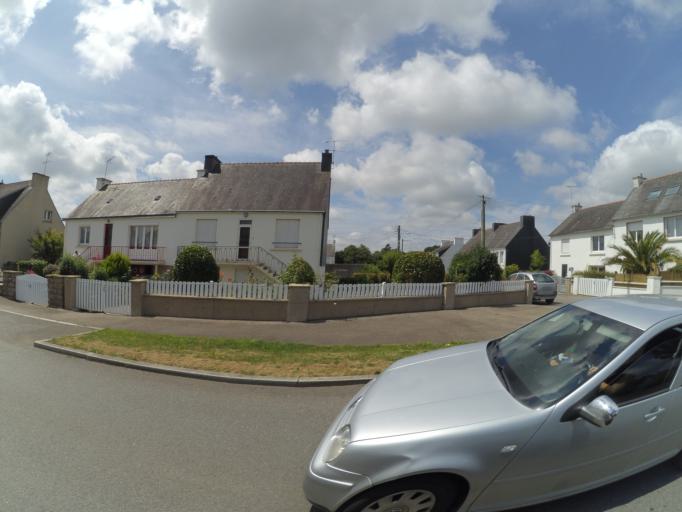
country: FR
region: Brittany
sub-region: Departement du Finistere
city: Rosporden
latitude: 47.9683
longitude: -3.8310
